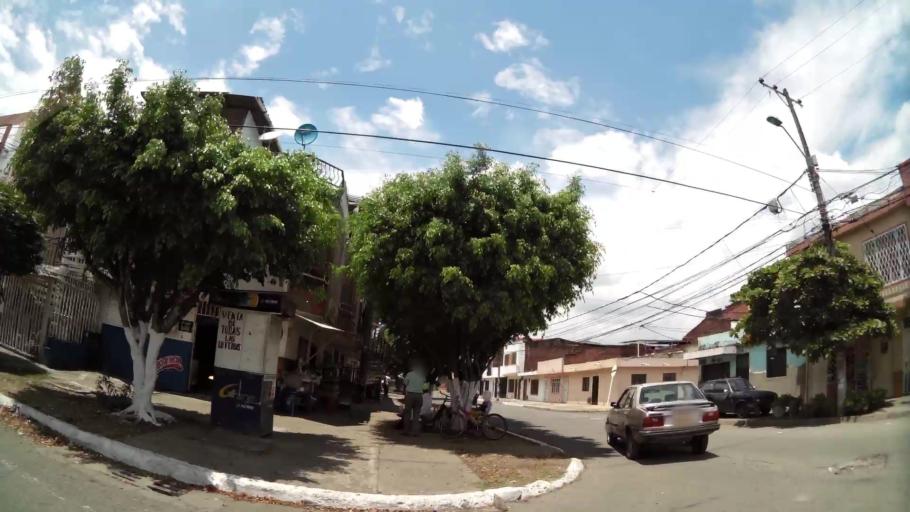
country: CO
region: Valle del Cauca
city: Cali
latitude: 3.4435
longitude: -76.5052
